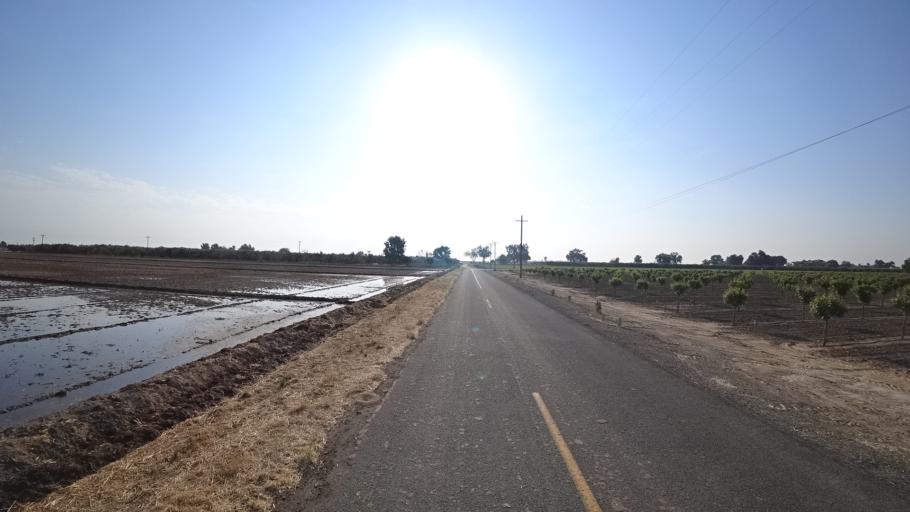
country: US
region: California
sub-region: Kings County
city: Lemoore
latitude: 36.3803
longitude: -119.7951
